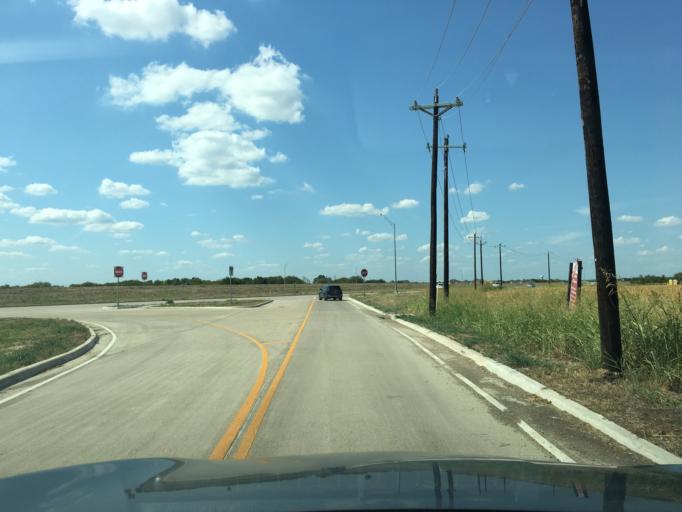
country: US
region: Texas
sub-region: Tarrant County
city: Mansfield
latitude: 32.5269
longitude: -97.0809
